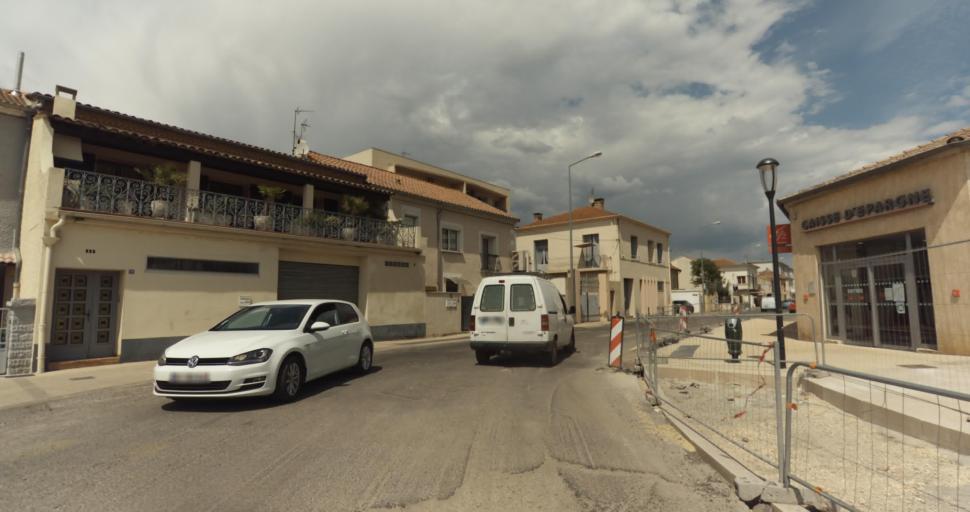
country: FR
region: Languedoc-Roussillon
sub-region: Departement du Gard
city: Nimes
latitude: 43.8431
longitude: 4.3816
